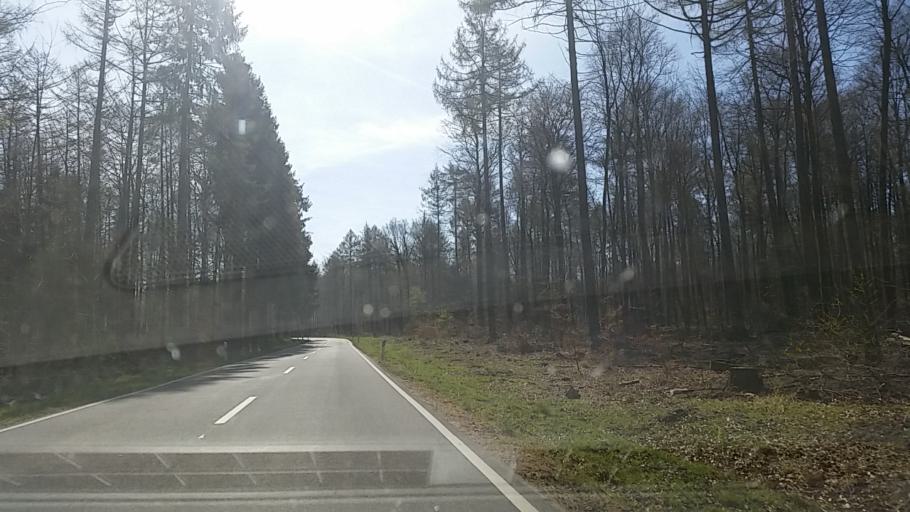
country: DE
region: Lower Saxony
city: Warberg
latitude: 52.1579
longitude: 10.9158
